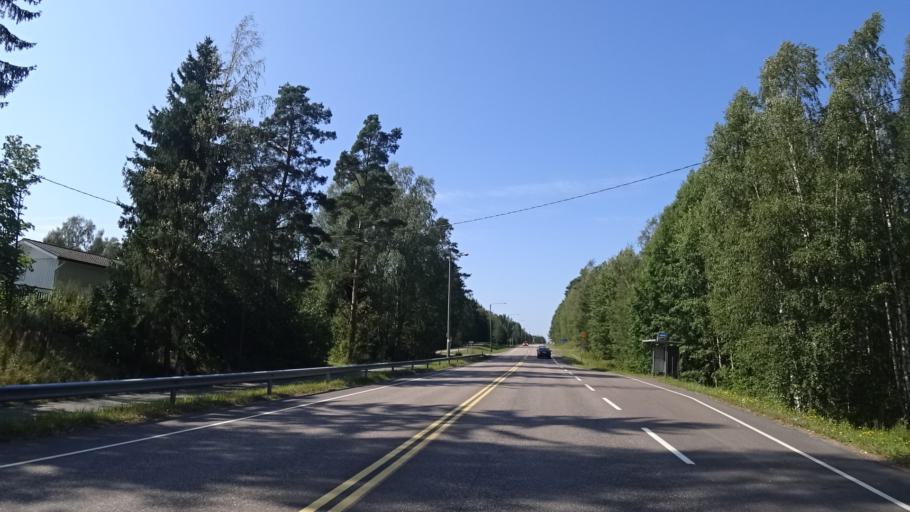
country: FI
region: Kymenlaakso
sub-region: Kotka-Hamina
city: Hamina
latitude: 60.5656
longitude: 27.0950
